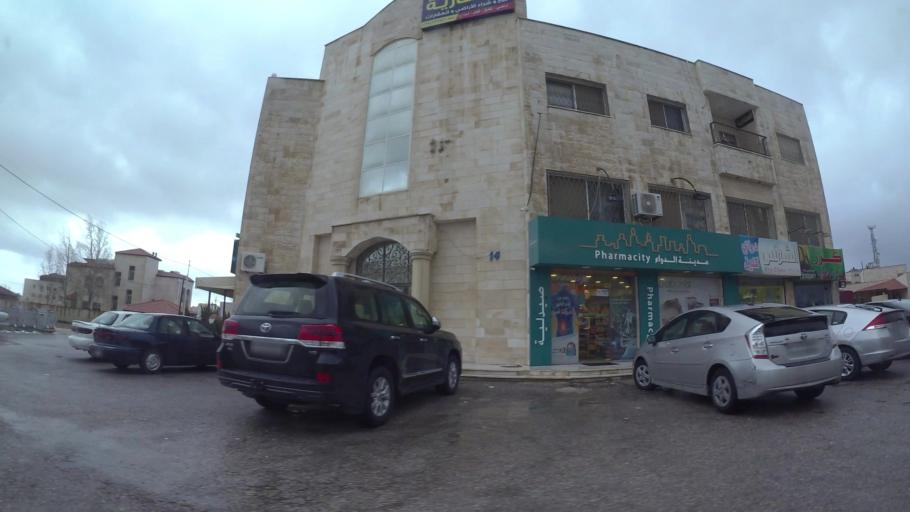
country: JO
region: Amman
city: Al Jubayhah
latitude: 32.0369
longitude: 35.8636
